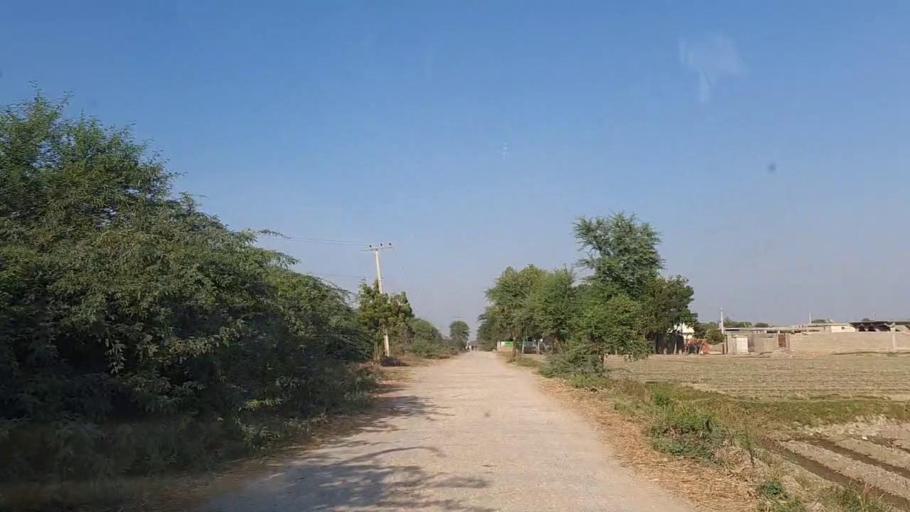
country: PK
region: Sindh
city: Thatta
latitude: 24.7585
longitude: 67.9625
